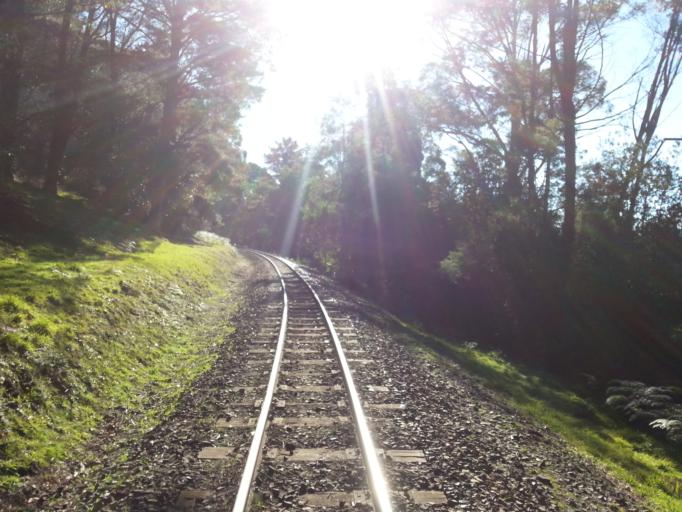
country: AU
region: Victoria
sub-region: Cardinia
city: Emerald
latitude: -37.9330
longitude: 145.4587
